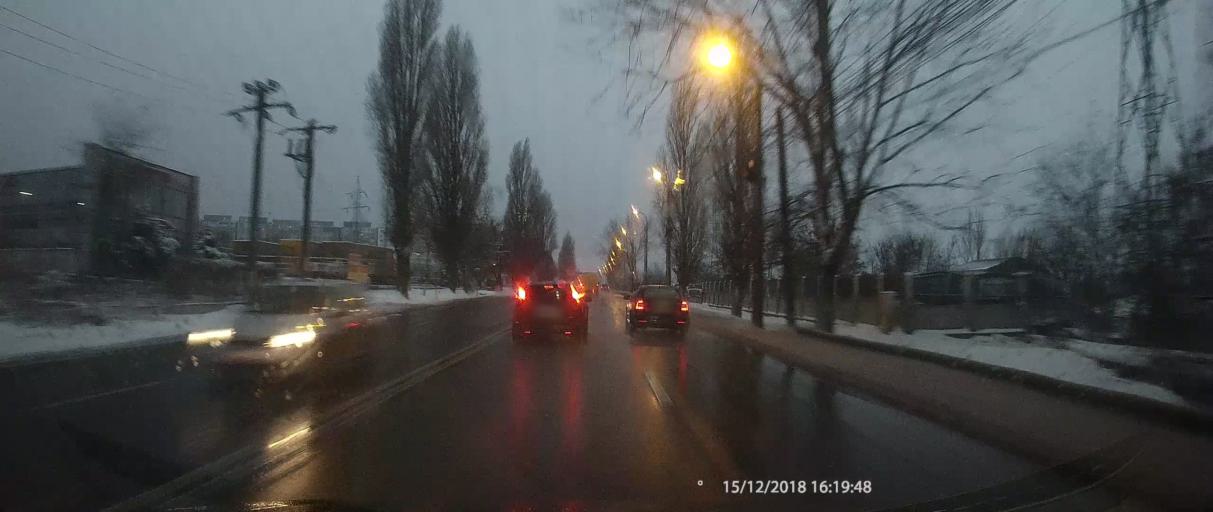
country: RO
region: Galati
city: Galati
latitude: 45.4178
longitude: 28.0049
